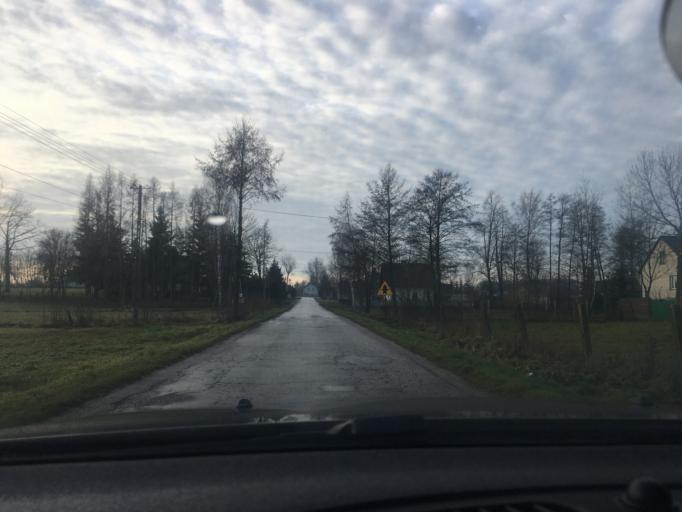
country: PL
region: Swietokrzyskie
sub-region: Powiat jedrzejowski
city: Imielno
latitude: 50.6296
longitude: 20.4054
